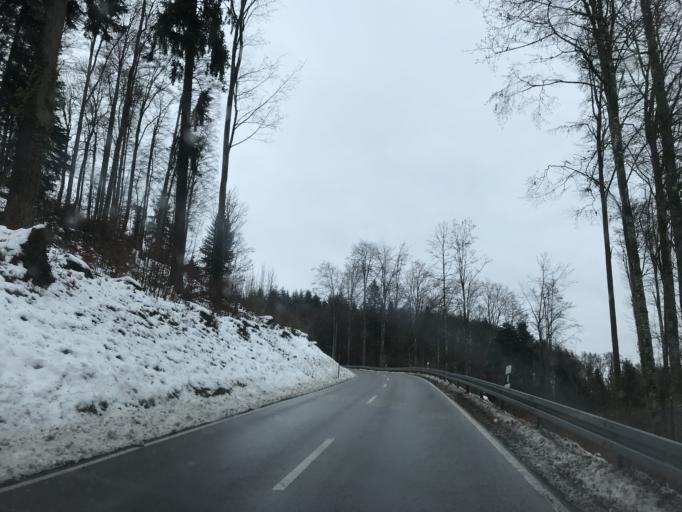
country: DE
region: Baden-Wuerttemberg
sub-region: Freiburg Region
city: Hasel
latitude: 47.6926
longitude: 7.8951
